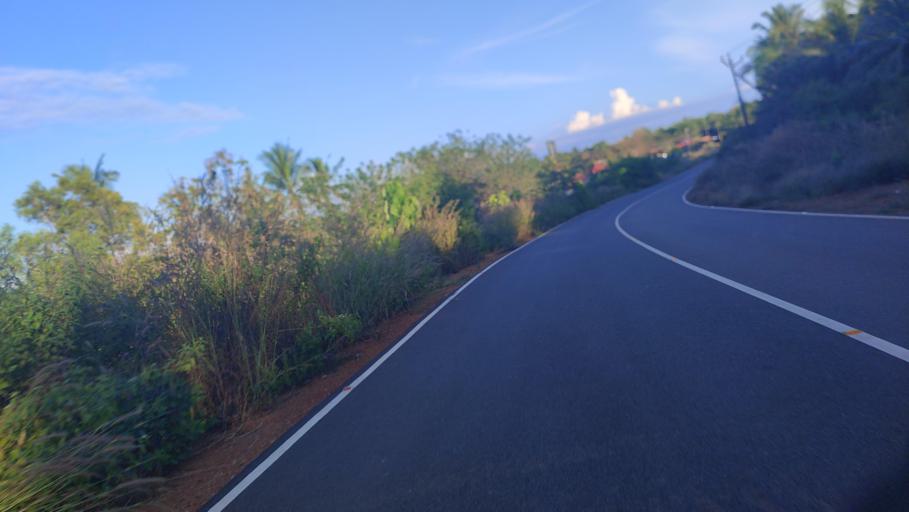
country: IN
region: Kerala
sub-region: Kasaragod District
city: Kasaragod
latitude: 12.4639
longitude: 75.0685
